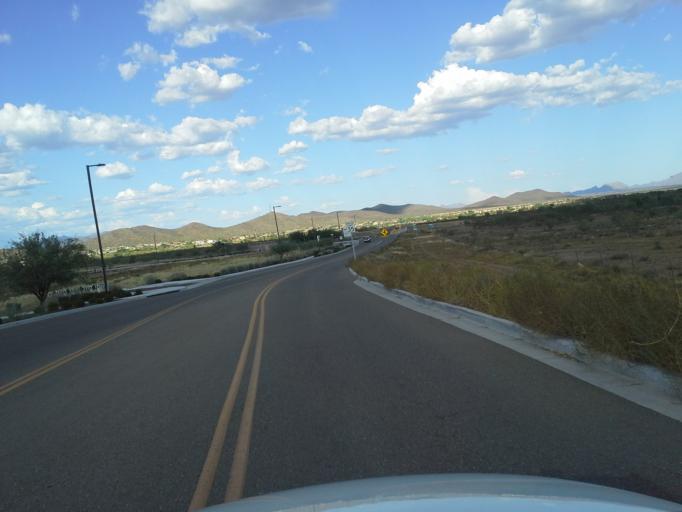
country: US
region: Arizona
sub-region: Maricopa County
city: Anthem
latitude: 33.7837
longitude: -112.1302
